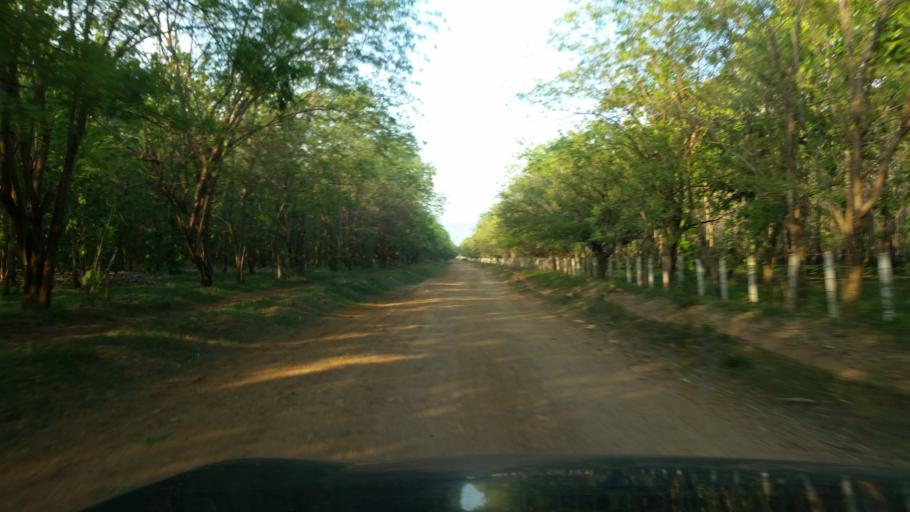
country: NI
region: Managua
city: Masachapa
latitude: 11.7733
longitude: -86.4901
